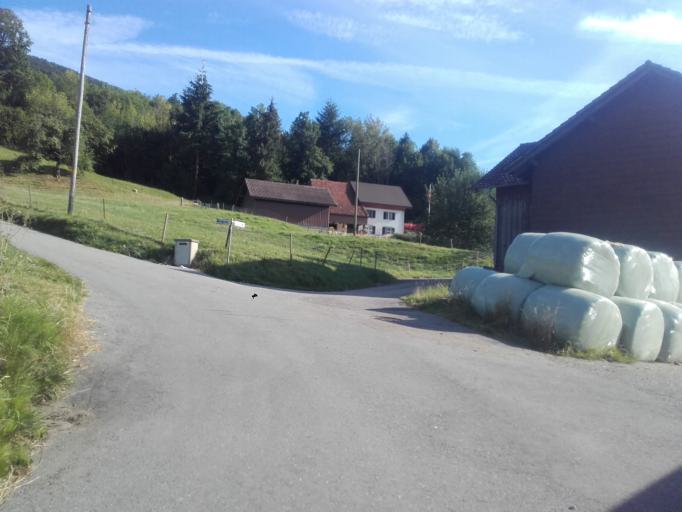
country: CH
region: Solothurn
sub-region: Bezirk Thal
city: Matzendorf
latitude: 47.3098
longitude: 7.6084
